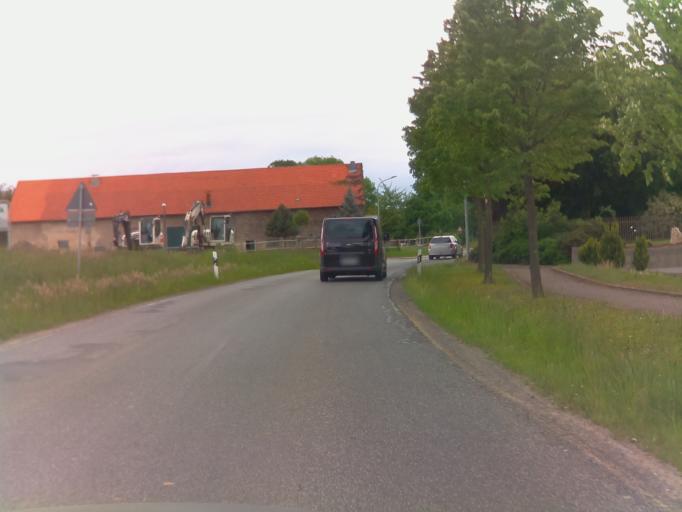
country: DE
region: Hesse
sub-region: Regierungsbezirk Kassel
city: Willingshausen
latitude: 50.8758
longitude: 9.1954
